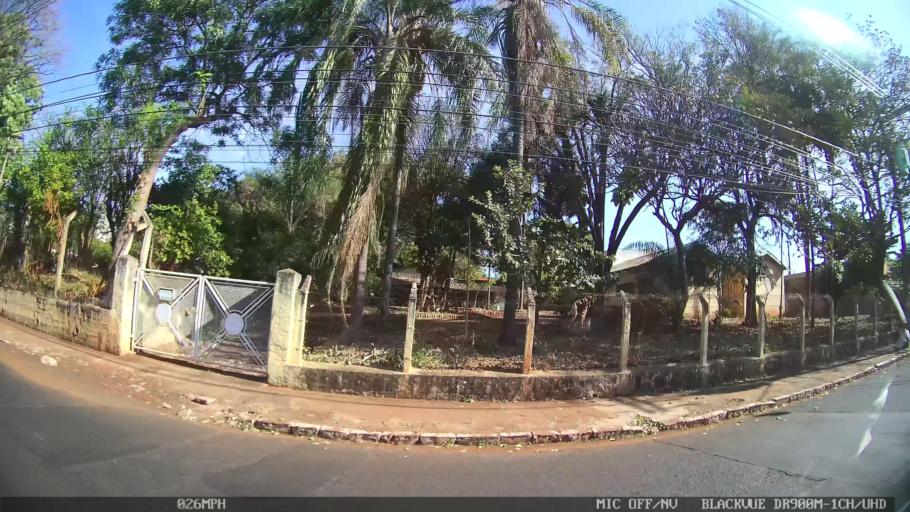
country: BR
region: Sao Paulo
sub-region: Ribeirao Preto
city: Ribeirao Preto
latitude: -21.1717
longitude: -47.7877
